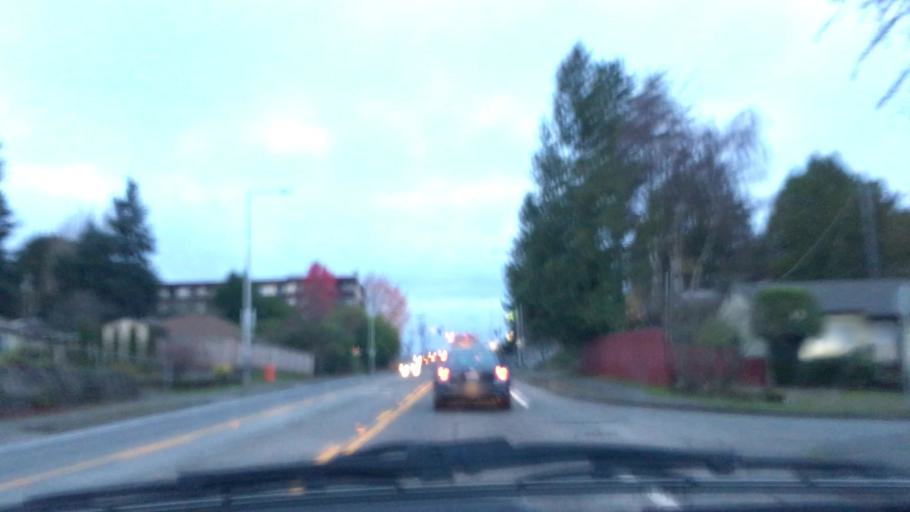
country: US
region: Washington
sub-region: King County
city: White Center
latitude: 47.5175
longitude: -122.3743
